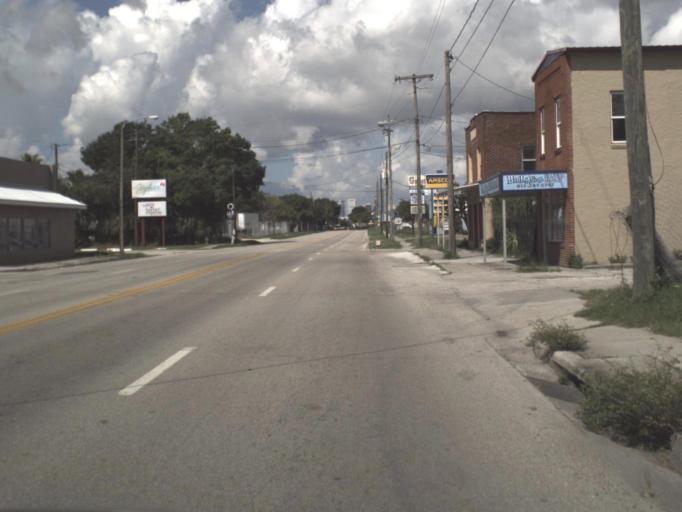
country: US
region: Florida
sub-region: Hillsborough County
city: East Lake-Orient Park
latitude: 27.9616
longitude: -82.4030
